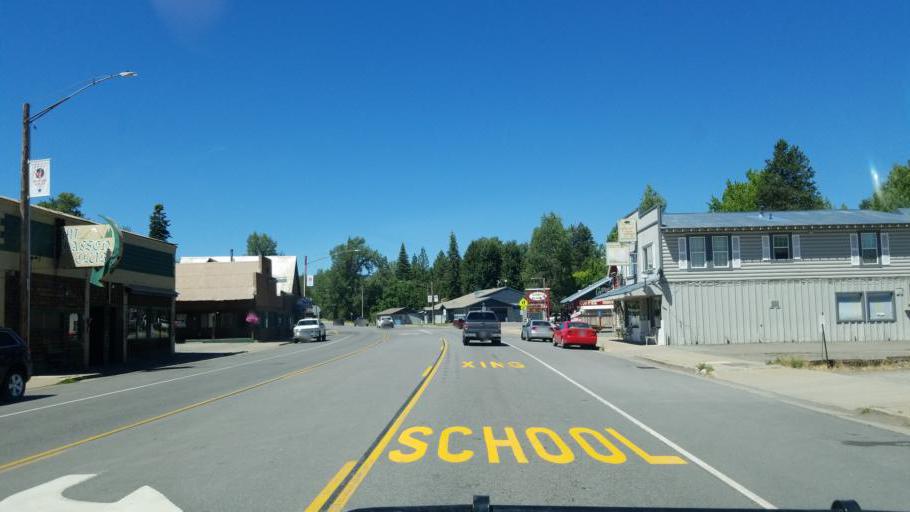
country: US
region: California
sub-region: Plumas County
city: Chester
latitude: 40.3119
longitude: -121.2259
